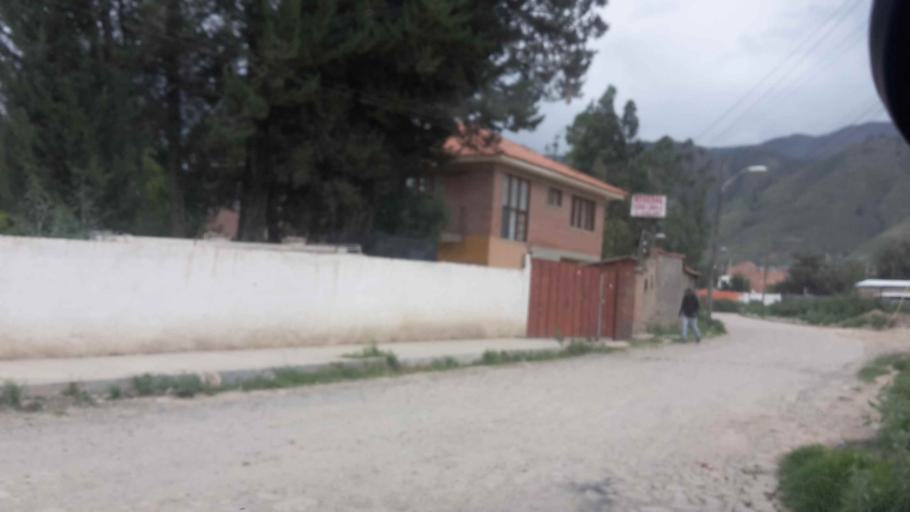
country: BO
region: Cochabamba
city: Cochabamba
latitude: -17.3342
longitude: -66.2222
